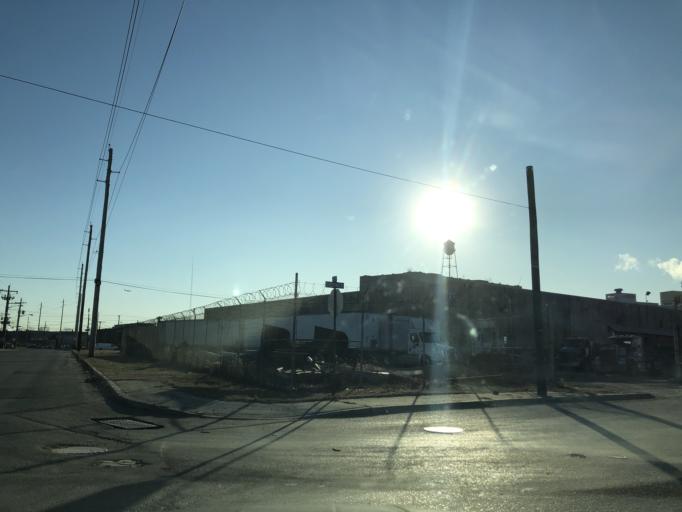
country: US
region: New Jersey
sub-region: Camden County
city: Camden
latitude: 39.9318
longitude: -75.1276
